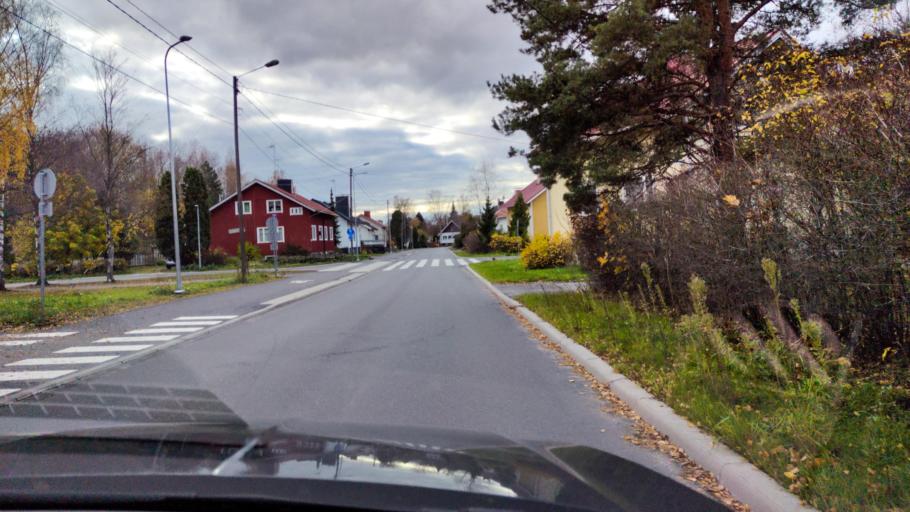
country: FI
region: Varsinais-Suomi
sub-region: Turku
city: Turku
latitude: 60.4673
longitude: 22.2567
